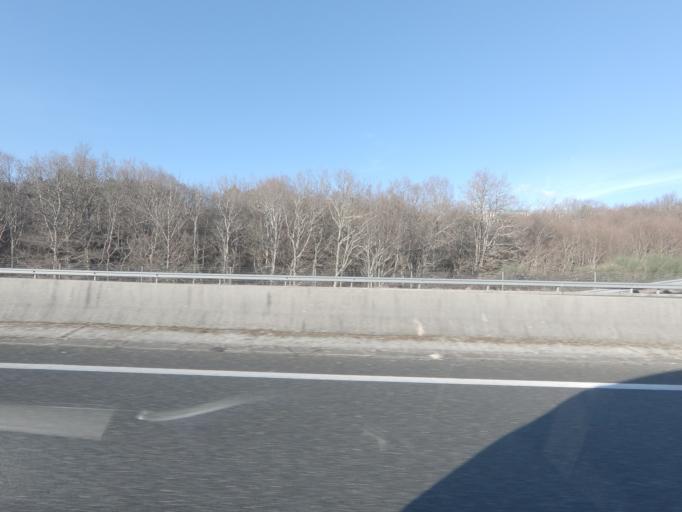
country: ES
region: Galicia
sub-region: Provincia de Pontevedra
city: Lalin
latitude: 42.6713
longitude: -8.1555
